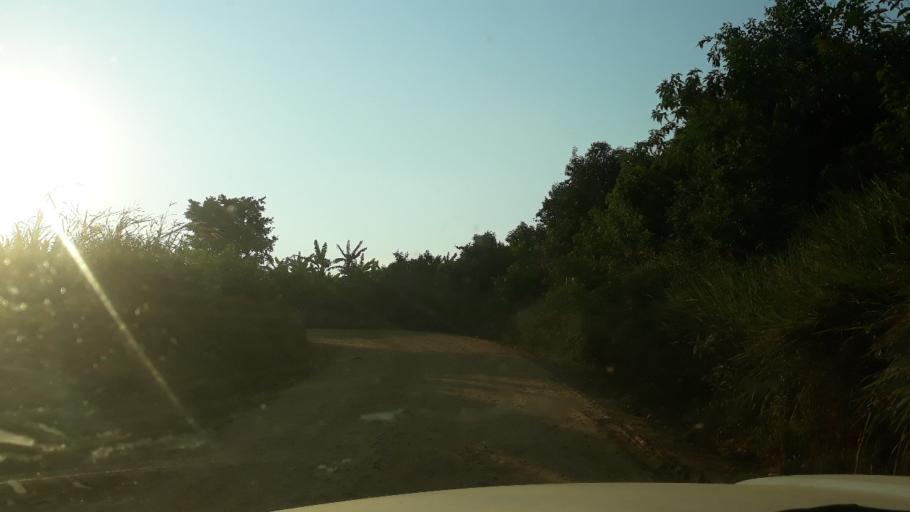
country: RW
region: Western Province
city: Cyangugu
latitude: -2.7013
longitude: 28.9197
